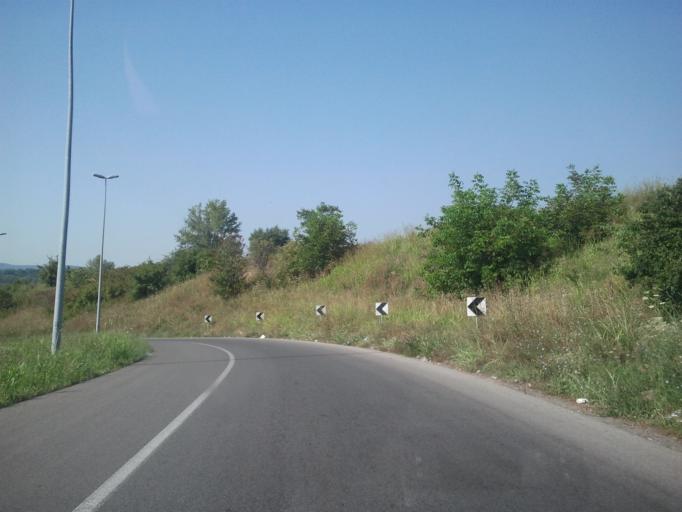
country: RS
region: Autonomna Pokrajina Vojvodina
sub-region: Juznobacki Okrug
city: Petrovaradin
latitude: 45.2239
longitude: 19.8697
